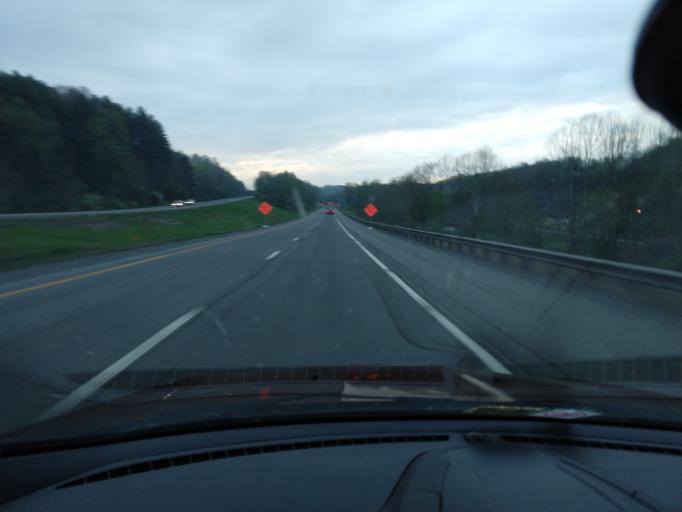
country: US
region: West Virginia
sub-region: Braxton County
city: Sutton
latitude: 38.6885
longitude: -80.6931
